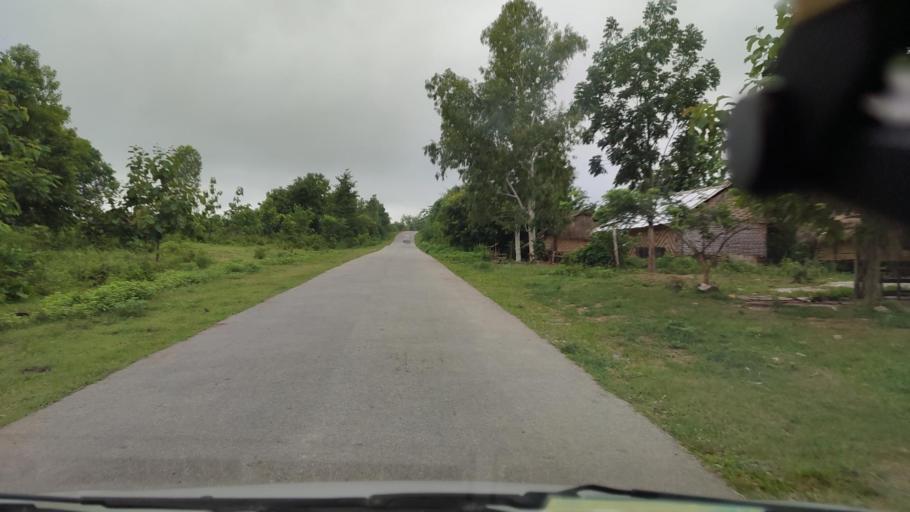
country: MM
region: Mandalay
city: Nay Pyi Taw
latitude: 19.9943
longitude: 95.9341
